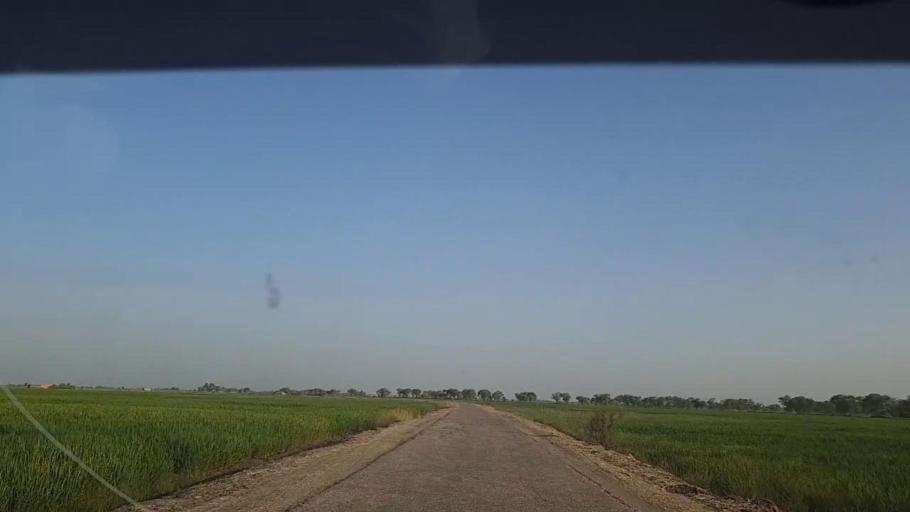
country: PK
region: Sindh
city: Thul
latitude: 28.1879
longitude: 68.8732
